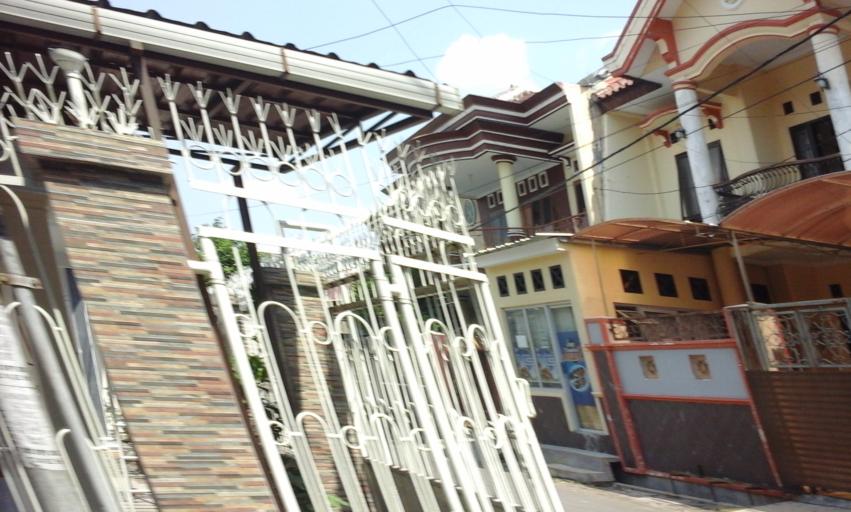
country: ID
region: East Java
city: Sumbersari Wetan
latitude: -8.1712
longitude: 113.7133
